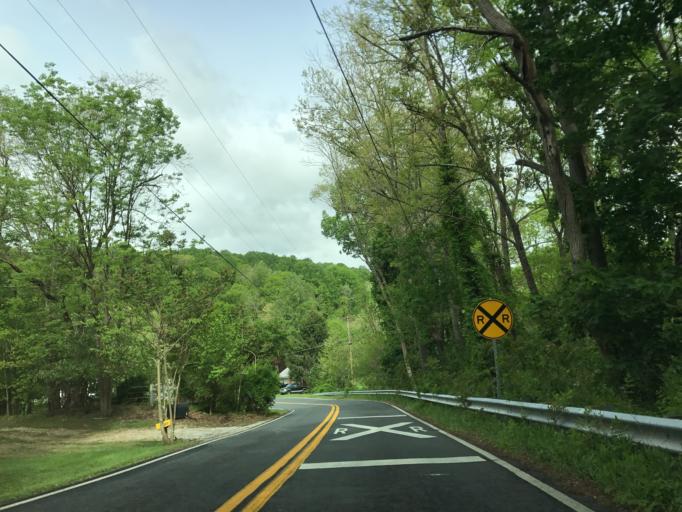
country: US
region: Maryland
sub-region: Carroll County
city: Hampstead
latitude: 39.5366
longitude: -76.8909
